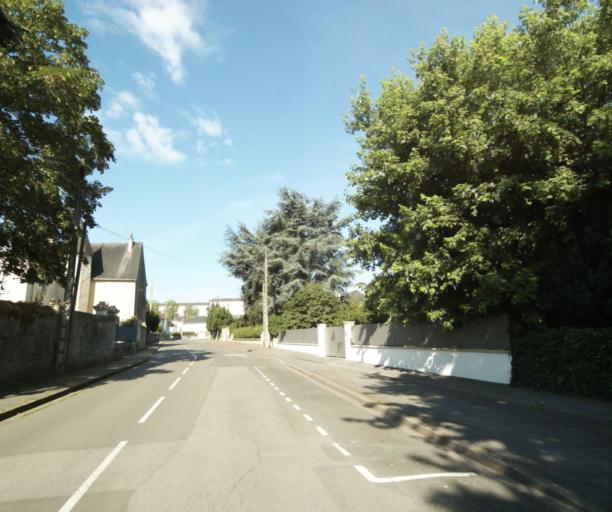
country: FR
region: Pays de la Loire
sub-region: Departement de la Mayenne
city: Laval
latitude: 48.0692
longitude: -0.7857
